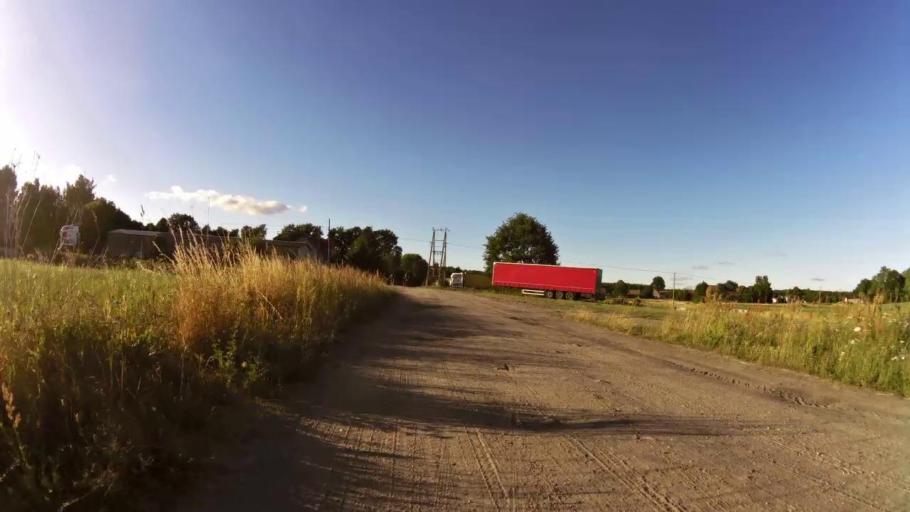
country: PL
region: West Pomeranian Voivodeship
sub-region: Powiat swidwinski
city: Swidwin
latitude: 53.7426
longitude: 15.8606
